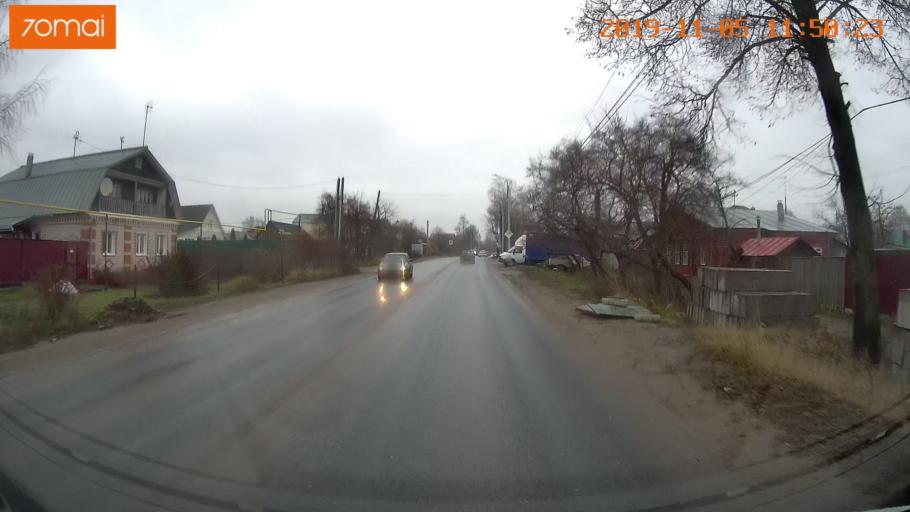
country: RU
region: Ivanovo
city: Bogorodskoye
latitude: 57.0069
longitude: 41.0157
